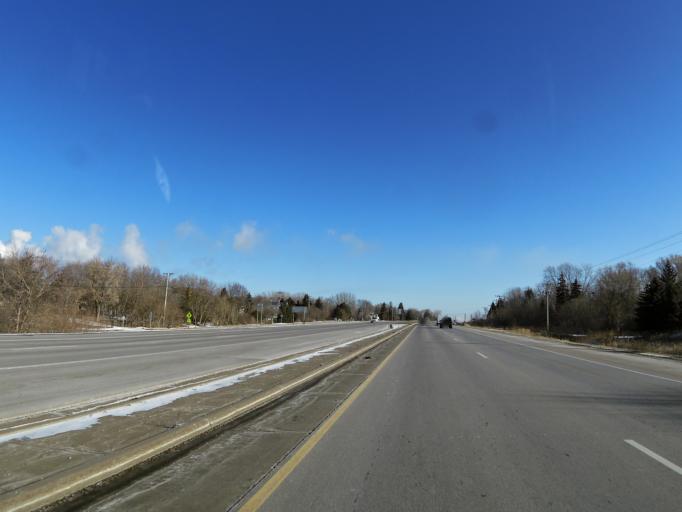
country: US
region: Minnesota
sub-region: Dakota County
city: Burnsville
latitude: 44.7940
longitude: -93.2394
